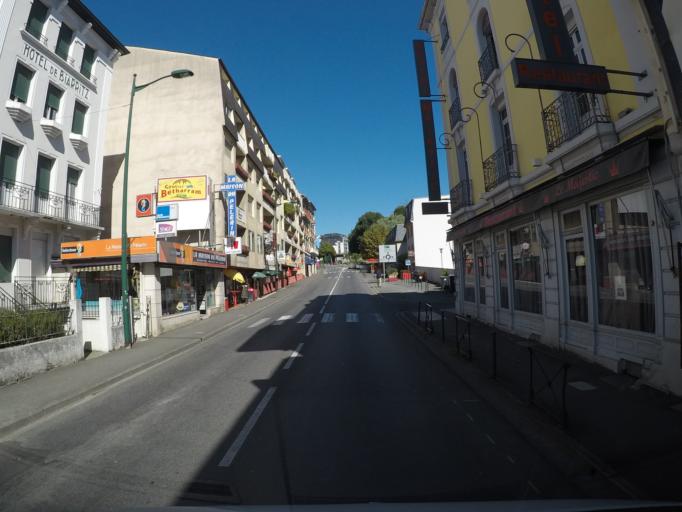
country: FR
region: Midi-Pyrenees
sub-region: Departement des Hautes-Pyrenees
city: Lourdes
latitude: 43.0982
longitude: -0.0456
